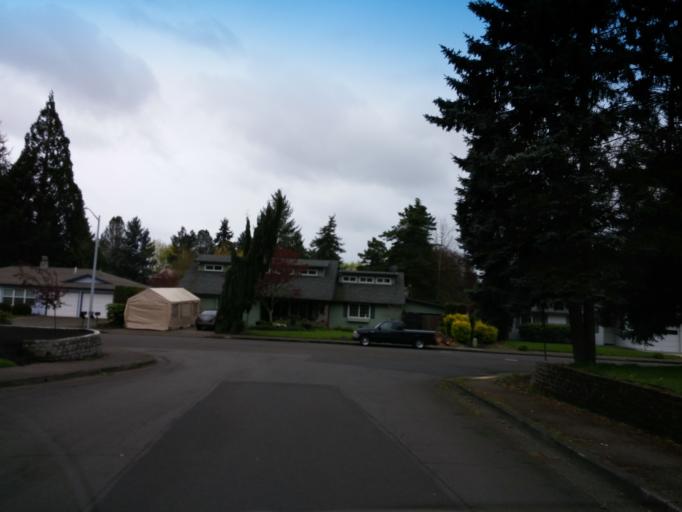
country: US
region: Oregon
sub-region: Washington County
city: Rockcreek
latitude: 45.5291
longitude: -122.8643
